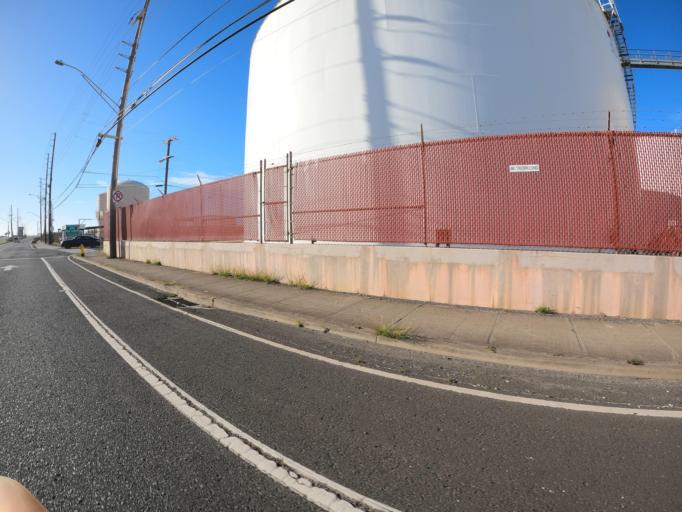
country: US
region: Hawaii
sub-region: Honolulu County
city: Honolulu
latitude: 21.3164
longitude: -157.8892
